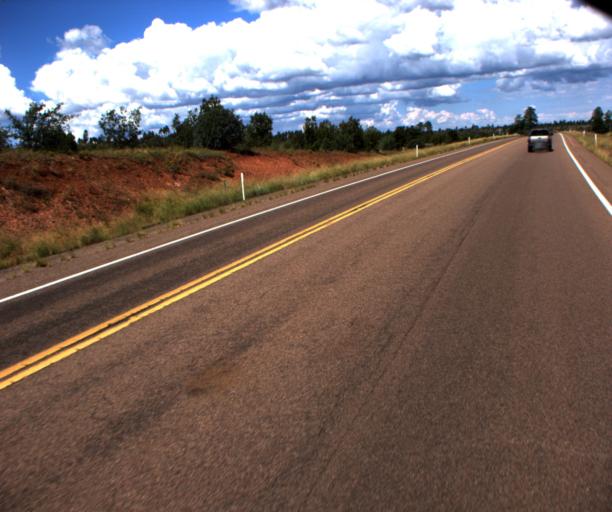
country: US
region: Arizona
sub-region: Navajo County
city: Heber-Overgaard
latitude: 34.3661
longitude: -110.4211
